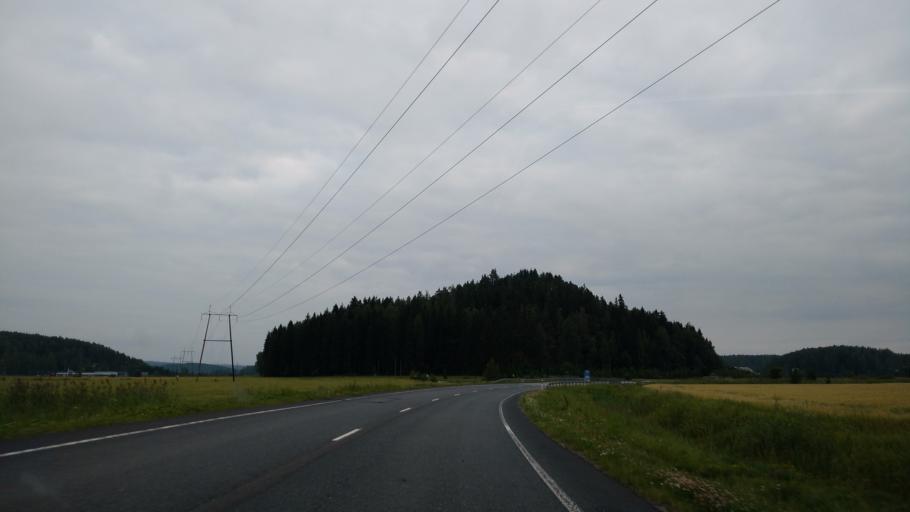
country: FI
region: Varsinais-Suomi
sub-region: Salo
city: Halikko
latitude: 60.3927
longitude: 23.0559
